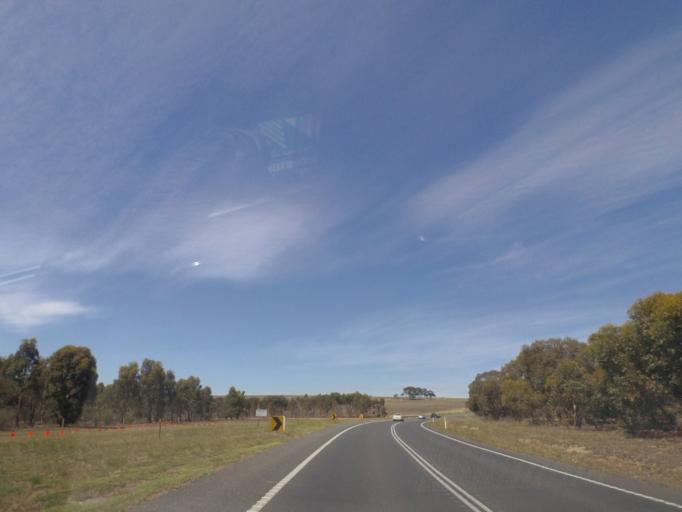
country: AU
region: Victoria
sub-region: Greater Geelong
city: Lara
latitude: -37.8840
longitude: 144.3781
